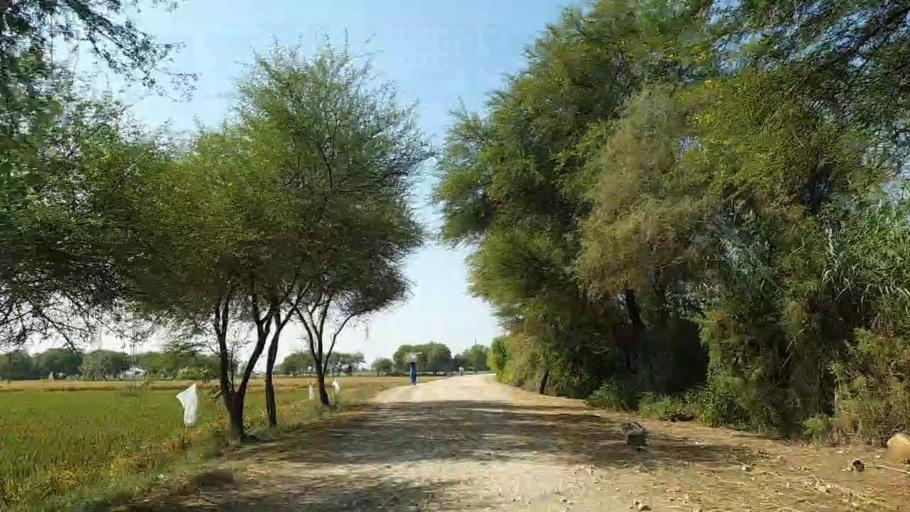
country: PK
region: Sindh
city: Chuhar Jamali
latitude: 24.4173
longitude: 68.0272
